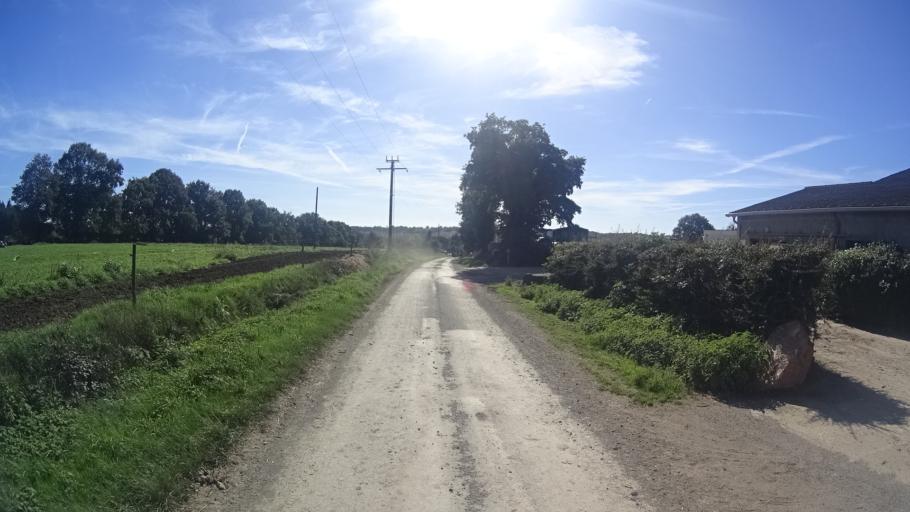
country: FR
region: Brittany
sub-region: Departement du Morbihan
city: Saint-Vincent-sur-Oust
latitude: 47.7332
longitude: -2.1732
